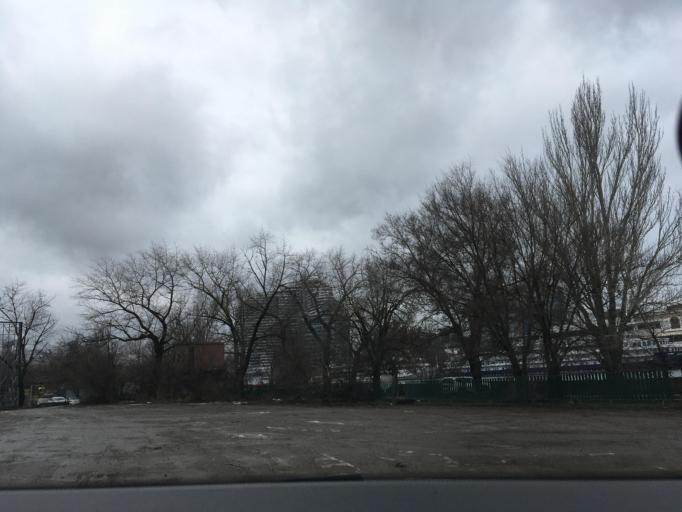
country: RU
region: Rostov
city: Rostov-na-Donu
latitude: 47.2113
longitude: 39.7122
